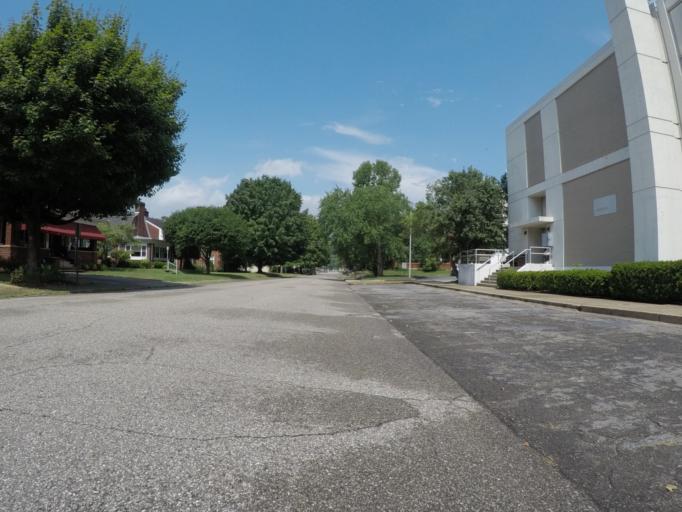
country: US
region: Kentucky
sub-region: Boyd County
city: Ashland
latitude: 38.4758
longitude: -82.6440
